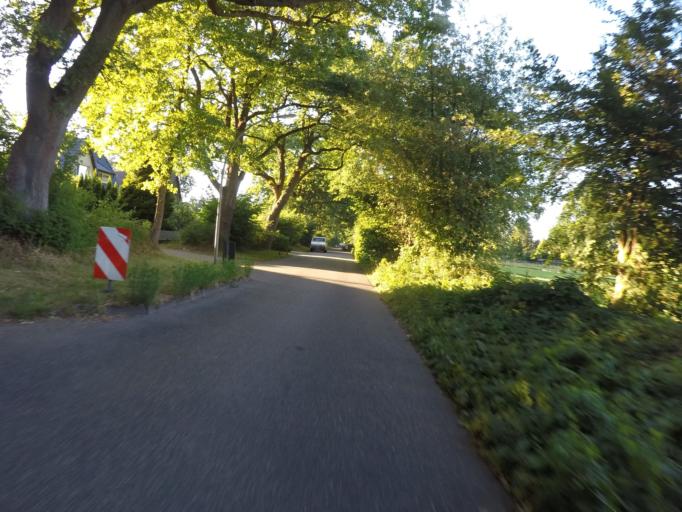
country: DE
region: Hamburg
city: Duvenstedt
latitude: 53.6963
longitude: 10.1110
